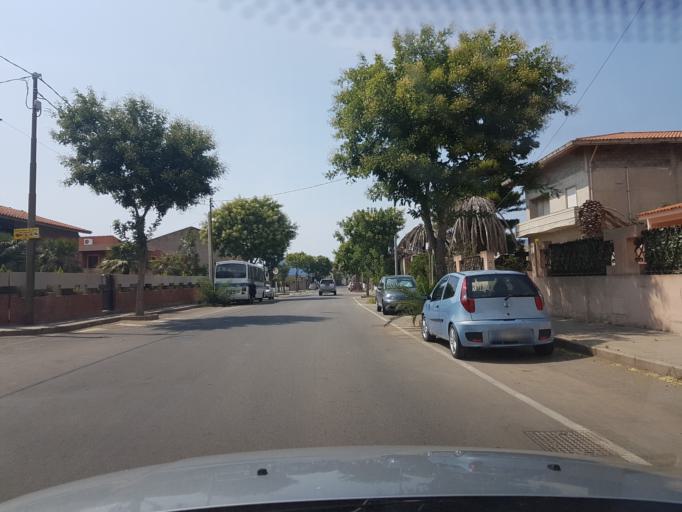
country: IT
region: Sardinia
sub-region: Provincia di Oristano
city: Cabras
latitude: 39.9233
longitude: 8.5407
